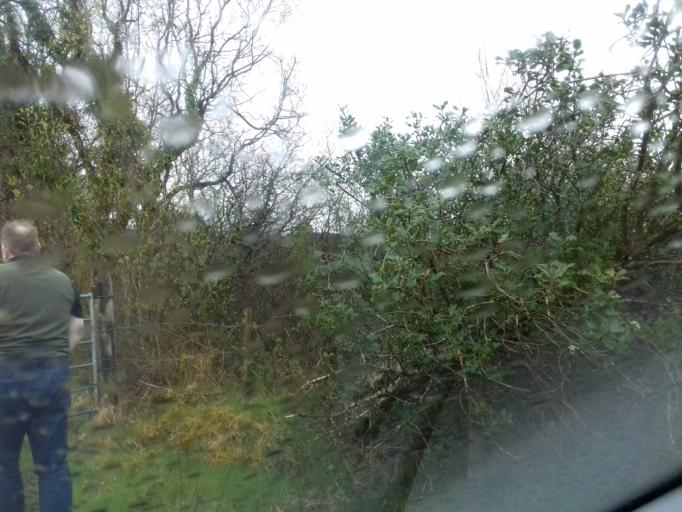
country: IE
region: Connaught
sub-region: County Leitrim
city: Manorhamilton
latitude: 54.2592
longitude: -7.9267
